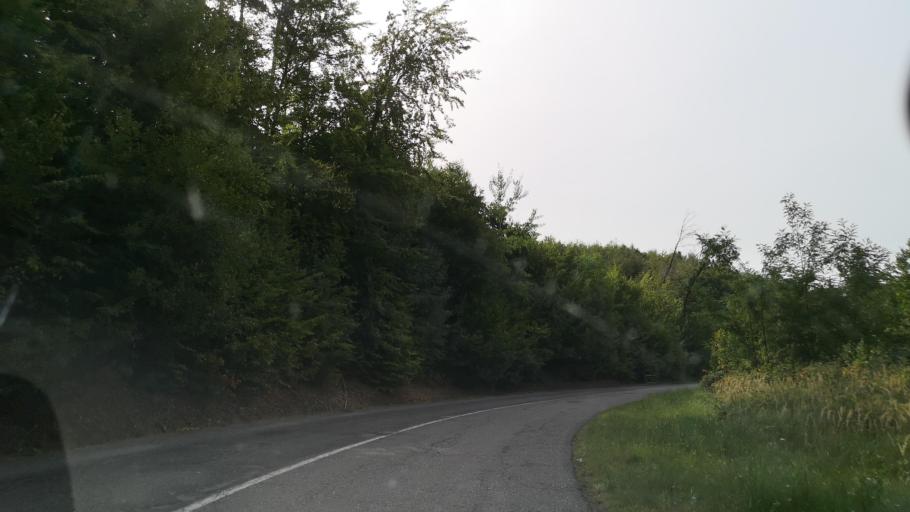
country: SK
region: Banskobystricky
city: Tisovec
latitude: 48.5678
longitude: 20.0289
